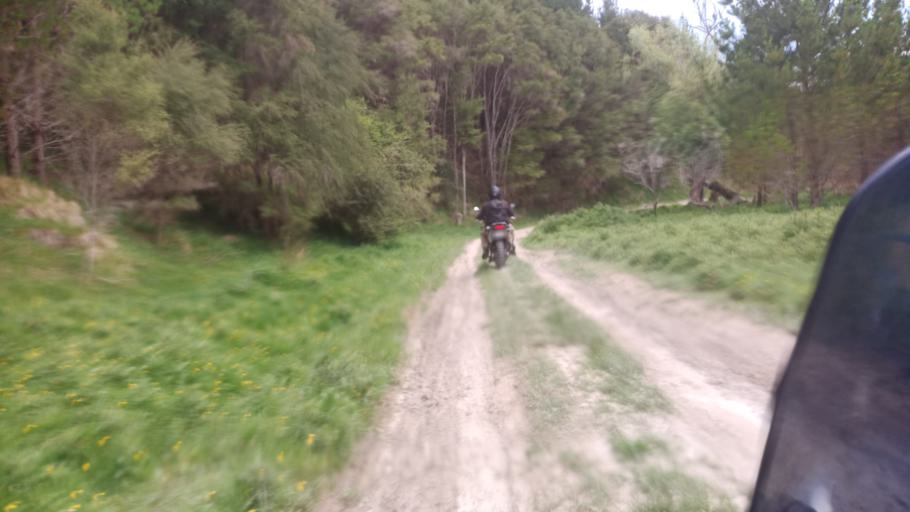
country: NZ
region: Gisborne
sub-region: Gisborne District
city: Gisborne
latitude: -38.4556
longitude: 177.9185
